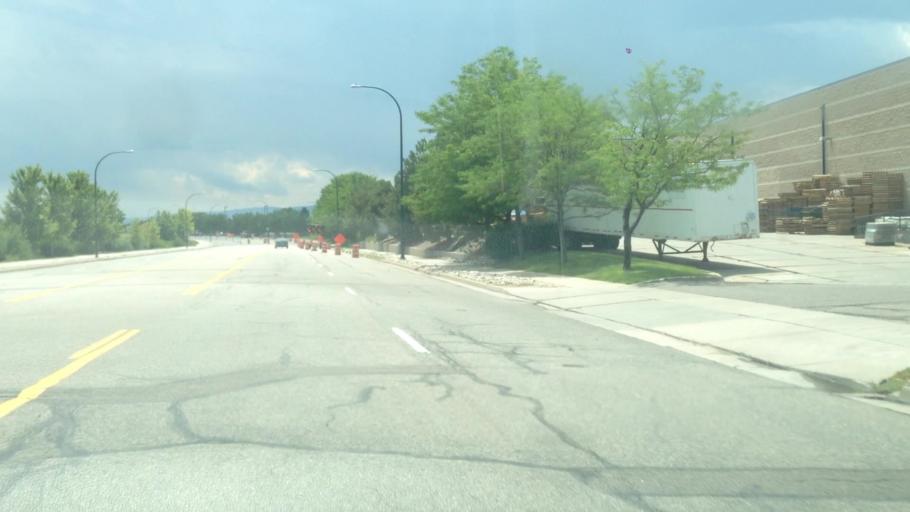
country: US
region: Colorado
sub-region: Jefferson County
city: Columbine
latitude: 39.6223
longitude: -105.0875
